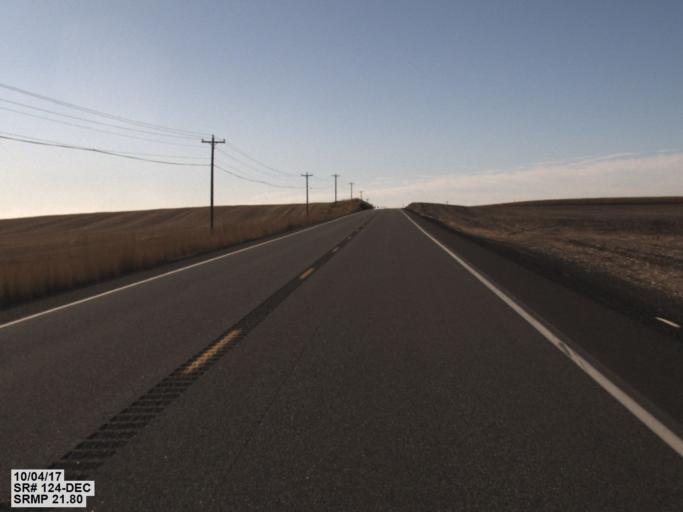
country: US
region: Washington
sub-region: Walla Walla County
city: Garrett
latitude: 46.2962
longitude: -118.6006
